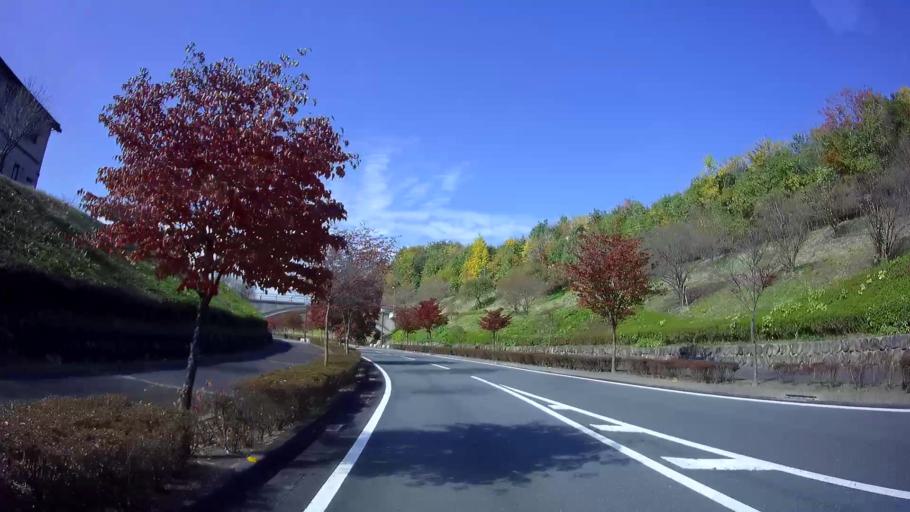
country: JP
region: Gunma
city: Annaka
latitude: 36.3567
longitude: 138.8505
